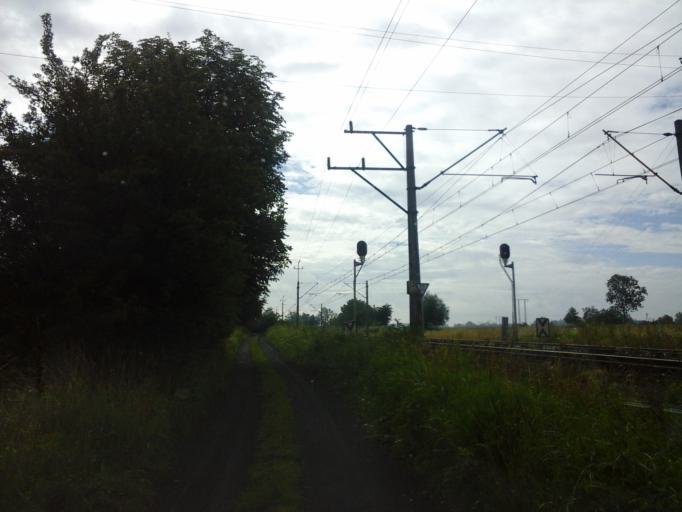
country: PL
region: West Pomeranian Voivodeship
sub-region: Powiat choszczenski
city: Choszczno
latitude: 53.1466
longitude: 15.4287
